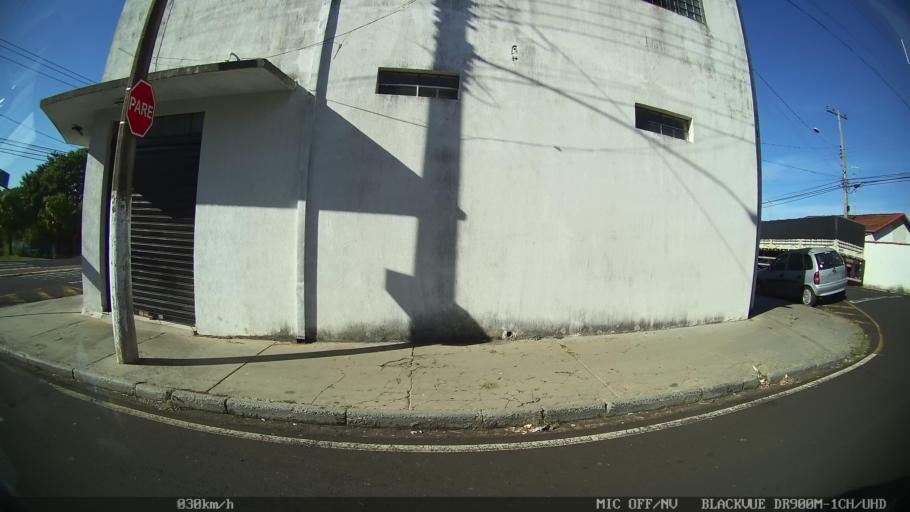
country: BR
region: Sao Paulo
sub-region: Franca
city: Franca
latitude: -20.5445
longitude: -47.4115
